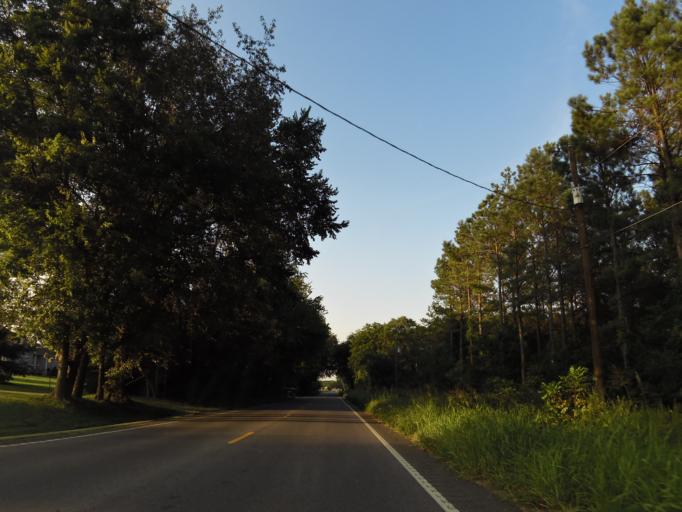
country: US
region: Tennessee
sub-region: Monroe County
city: Sweetwater
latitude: 35.5401
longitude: -84.5214
